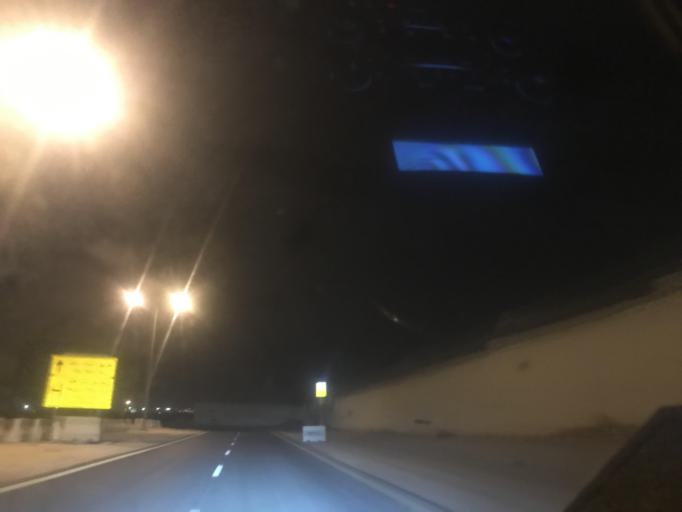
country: SA
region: Ar Riyad
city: Riyadh
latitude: 24.7641
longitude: 46.5890
